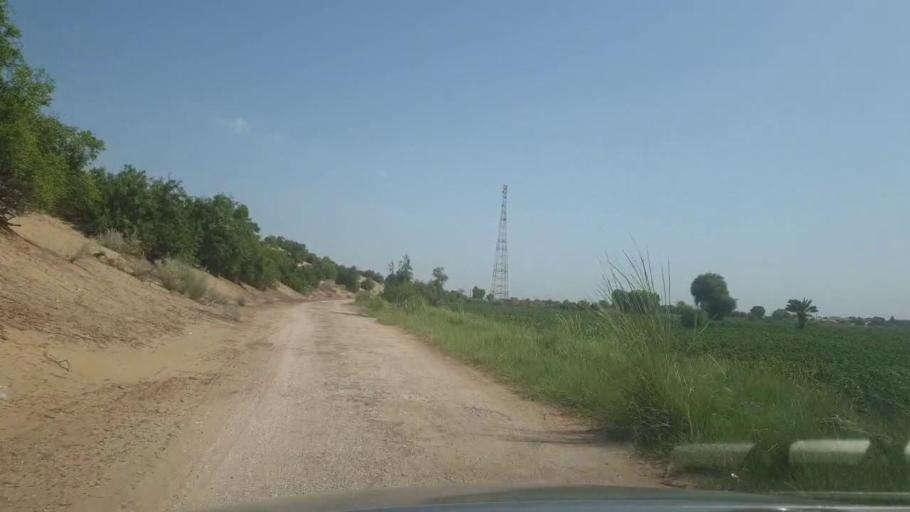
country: PK
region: Sindh
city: Khairpur
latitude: 27.3983
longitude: 69.0792
